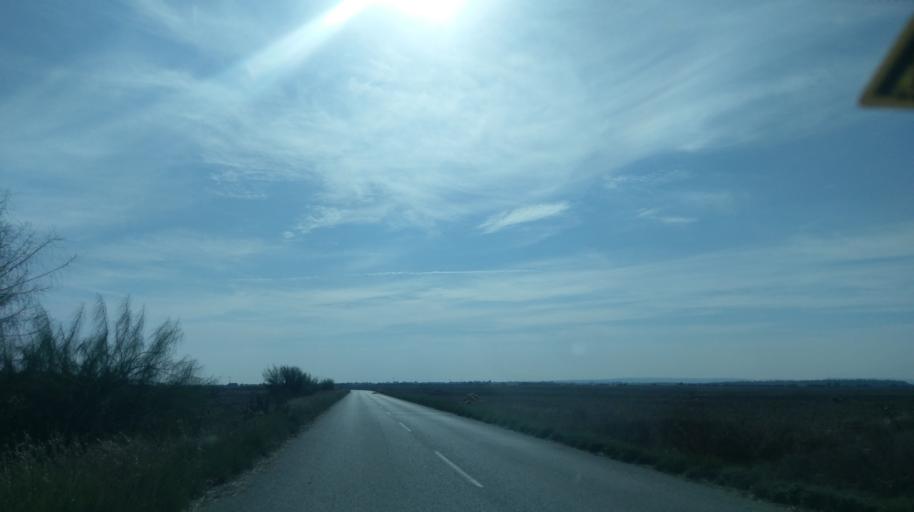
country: CY
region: Ammochostos
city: Lefkonoiko
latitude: 35.1974
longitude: 33.6957
